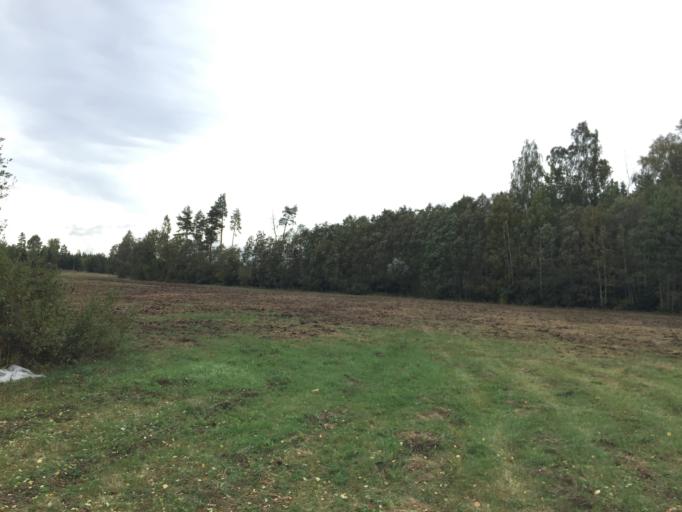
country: LV
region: Malpils
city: Malpils
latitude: 56.9330
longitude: 24.9456
